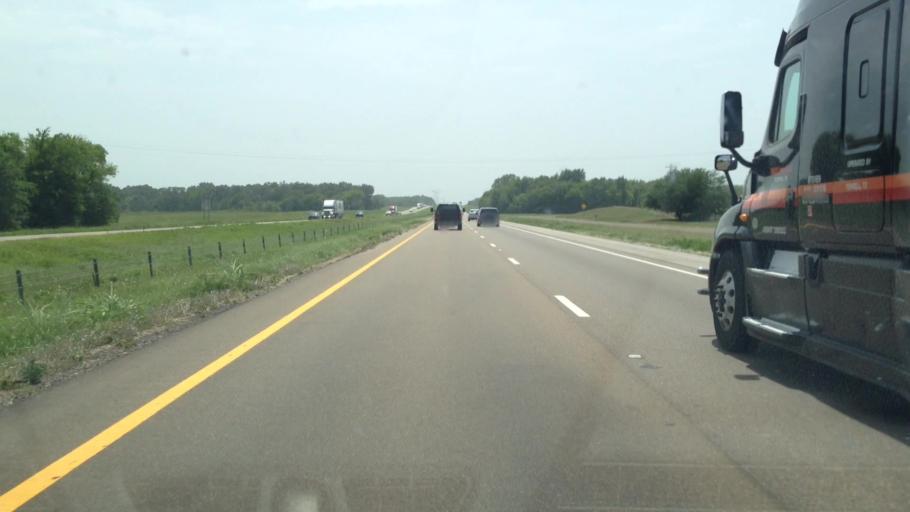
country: US
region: Texas
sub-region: Morris County
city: Omaha
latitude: 33.2508
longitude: -94.8495
